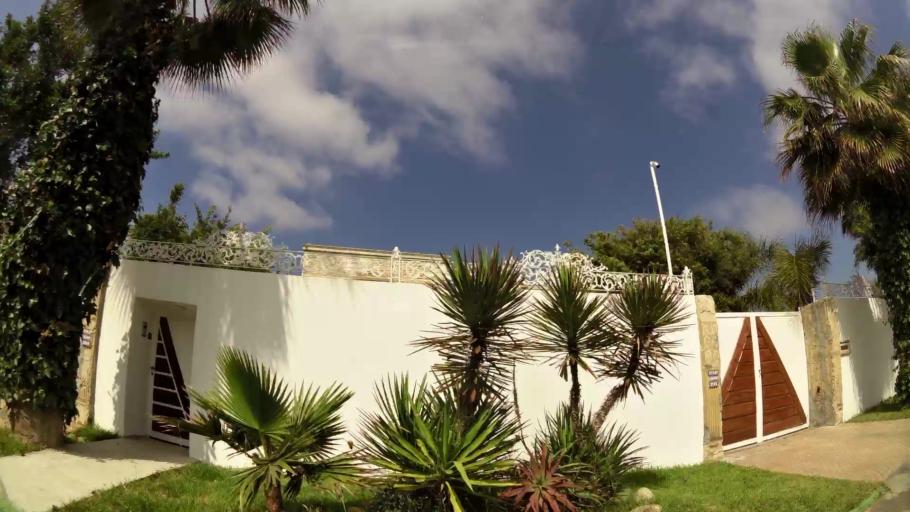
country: MA
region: Rabat-Sale-Zemmour-Zaer
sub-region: Rabat
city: Rabat
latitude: 33.9878
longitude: -6.8325
